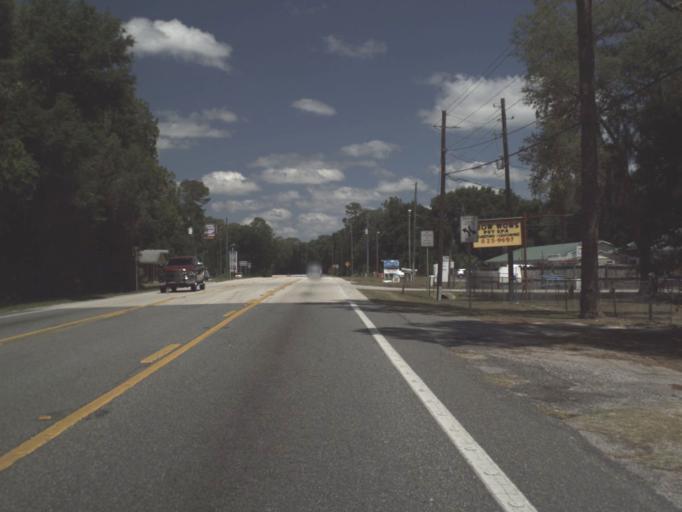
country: US
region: Florida
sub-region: Marion County
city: Silver Springs Shores
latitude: 29.1954
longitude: -81.9136
